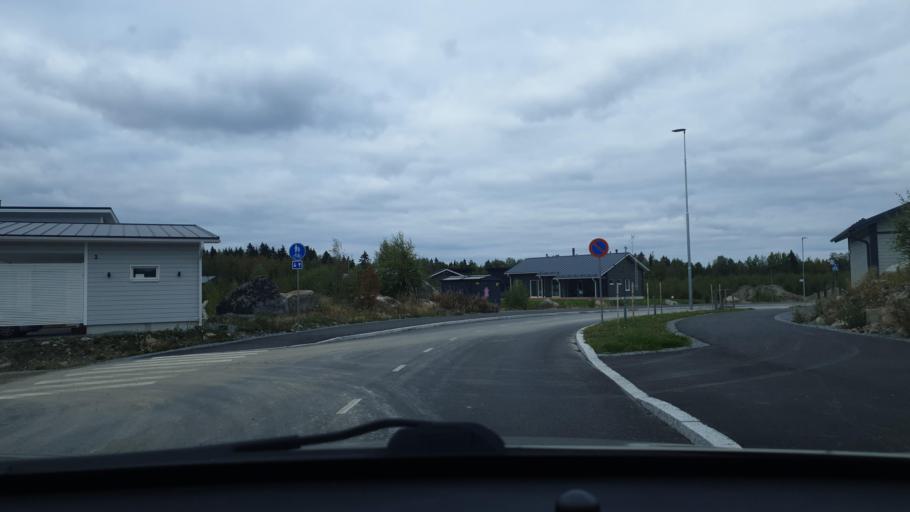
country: FI
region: Ostrobothnia
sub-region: Vaasa
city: Korsholm
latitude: 63.1302
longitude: 21.6514
